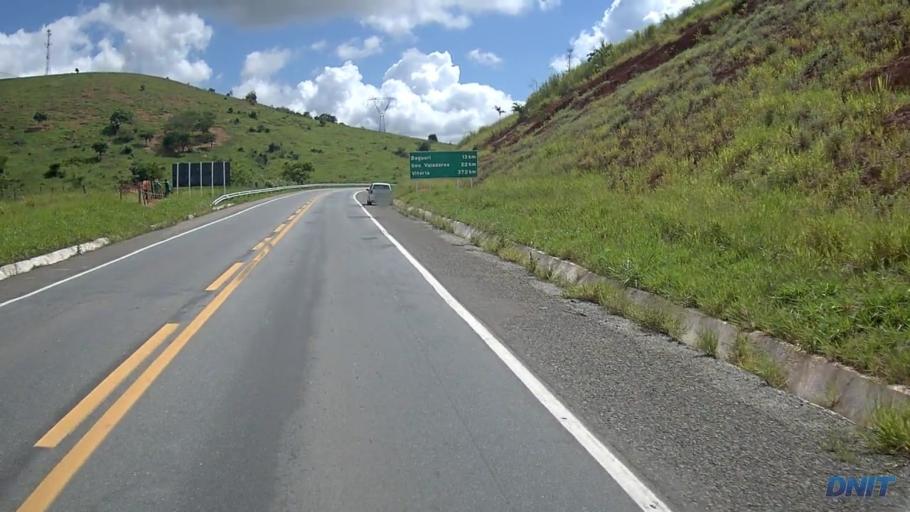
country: BR
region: Minas Gerais
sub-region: Governador Valadares
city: Governador Valadares
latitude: -19.0249
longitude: -42.1464
